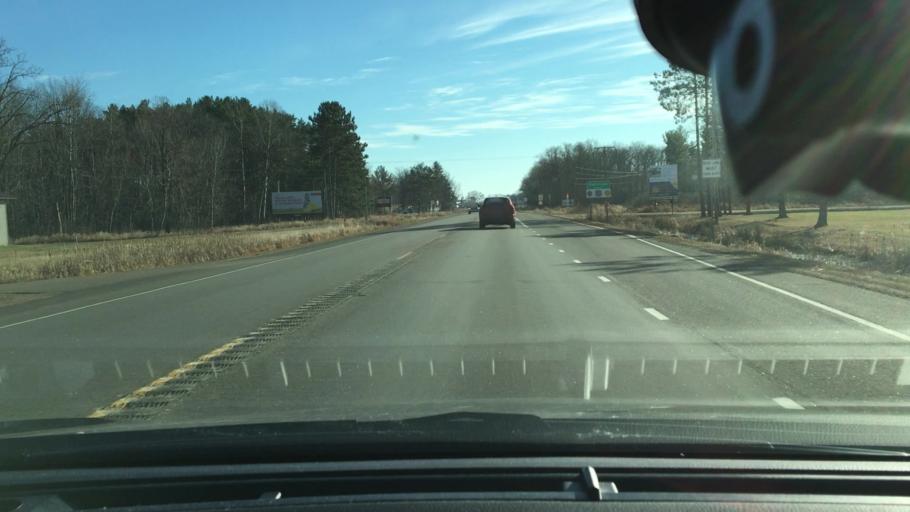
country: US
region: Minnesota
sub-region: Mille Lacs County
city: Vineland
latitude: 46.3022
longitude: -93.8288
